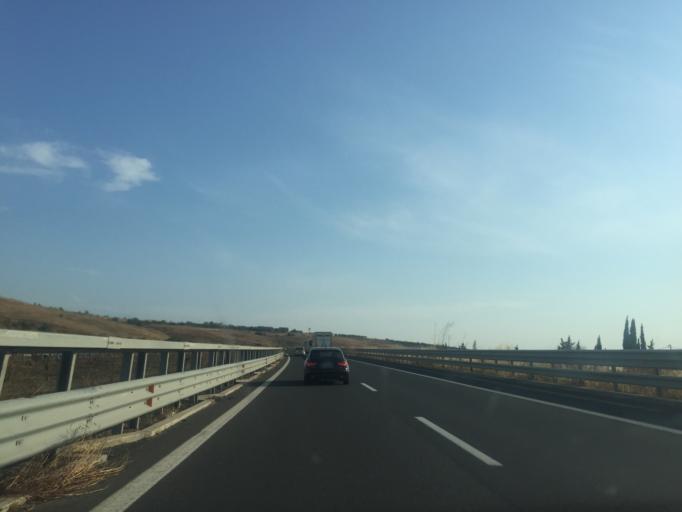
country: IT
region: Sicily
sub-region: Provincia di Siracusa
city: Carlentini
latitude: 37.3547
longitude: 15.0470
